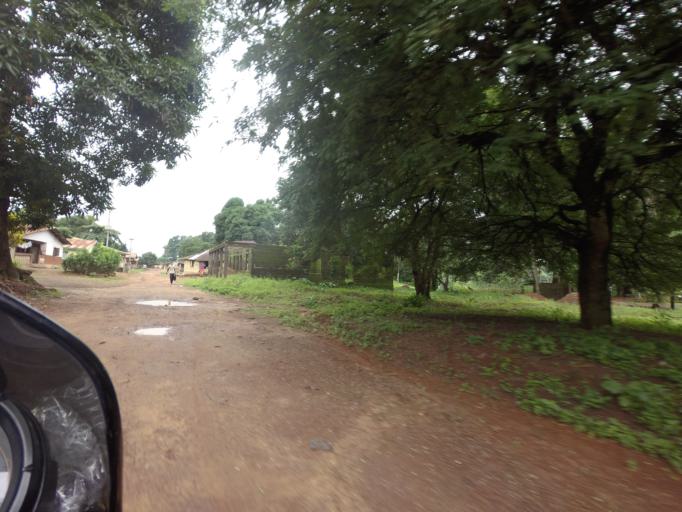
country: SL
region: Northern Province
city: Kambia
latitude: 9.1247
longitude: -12.9206
